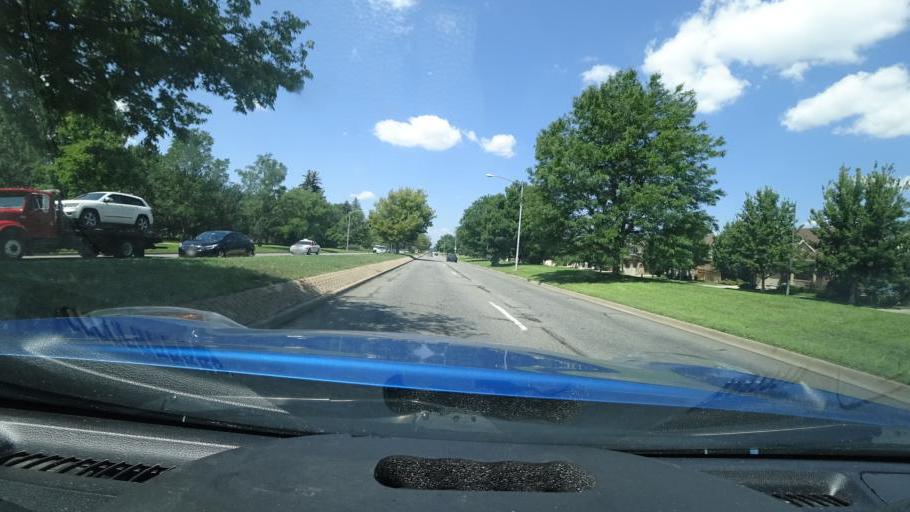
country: US
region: Colorado
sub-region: Arapahoe County
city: Glendale
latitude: 39.7113
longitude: -104.8970
